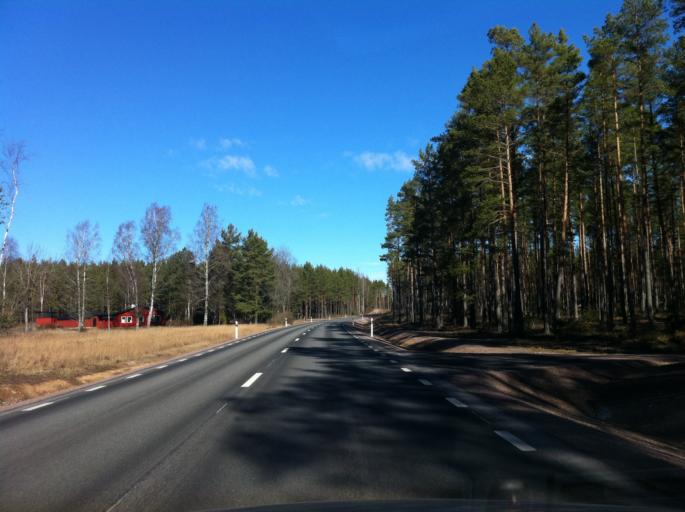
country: SE
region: Vaestra Goetaland
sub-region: Tibro Kommun
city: Tibro
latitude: 58.4450
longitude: 14.1866
